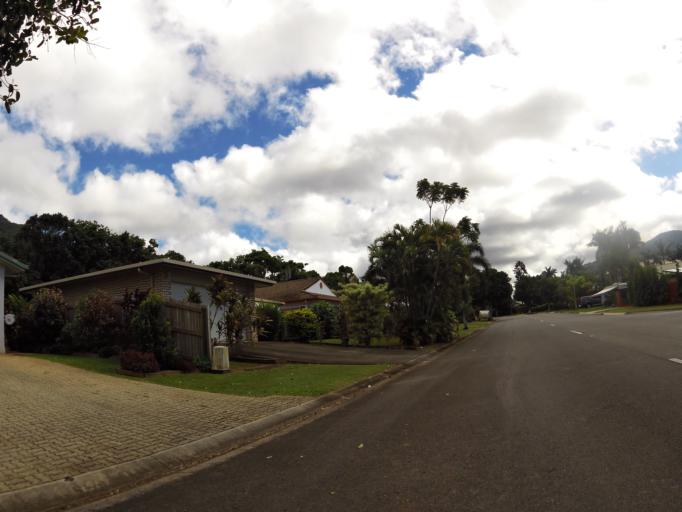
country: AU
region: Queensland
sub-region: Cairns
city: Redlynch
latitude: -16.8812
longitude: 145.6928
